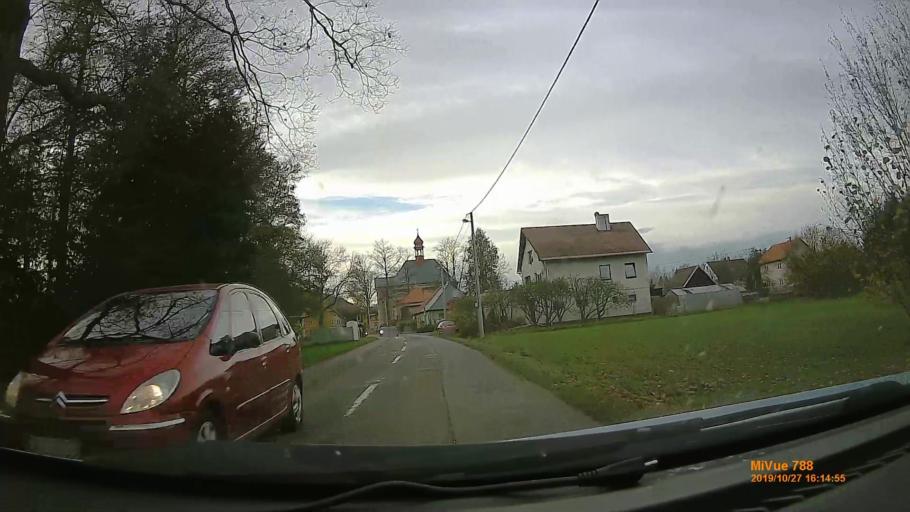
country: PL
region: Lower Silesian Voivodeship
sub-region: Powiat klodzki
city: Radkow
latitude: 50.5567
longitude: 16.3888
